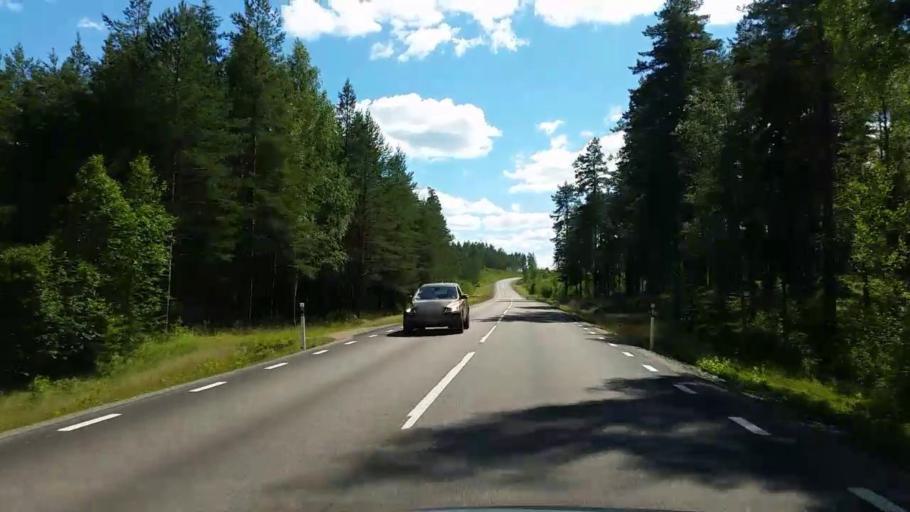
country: SE
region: Dalarna
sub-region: Faluns Kommun
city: Falun
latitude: 60.6934
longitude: 15.7274
